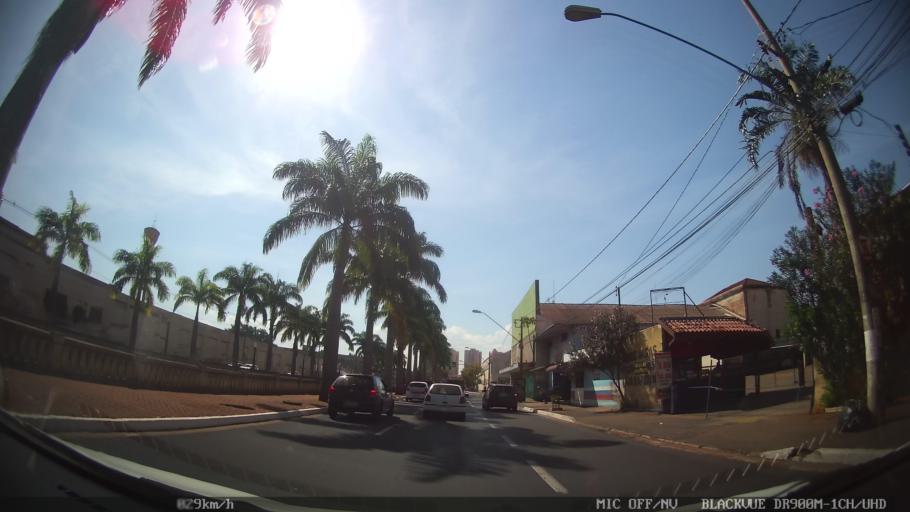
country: BR
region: Sao Paulo
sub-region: Ribeirao Preto
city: Ribeirao Preto
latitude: -21.1716
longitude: -47.8123
